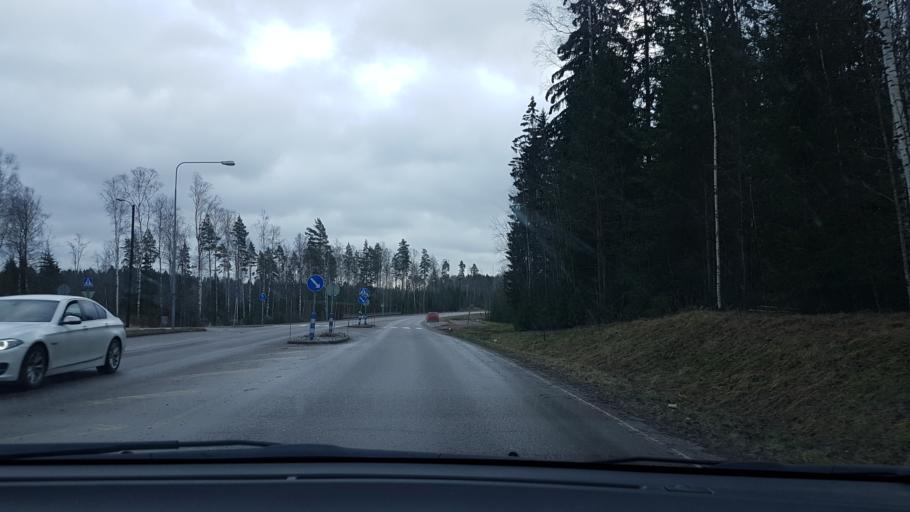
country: FI
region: Uusimaa
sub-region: Helsinki
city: Tuusula
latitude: 60.3752
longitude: 25.0583
